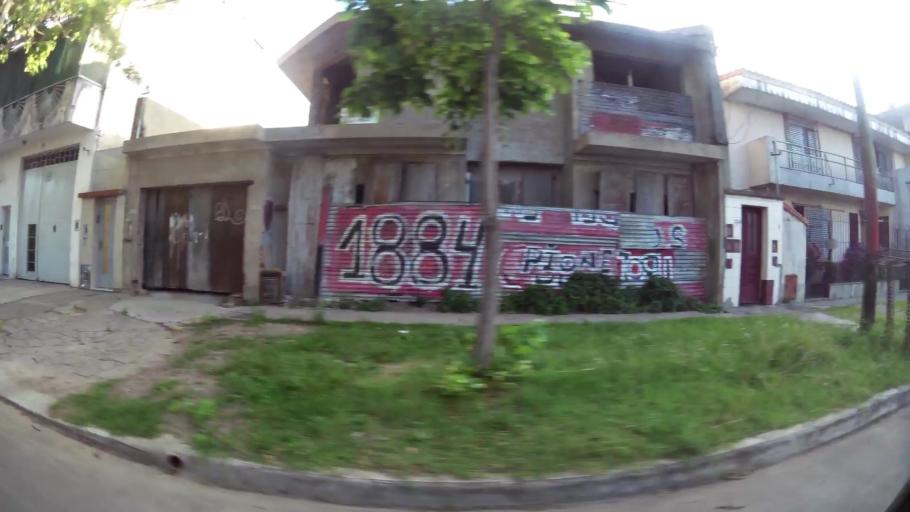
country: AR
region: Santa Fe
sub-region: Departamento de Rosario
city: Rosario
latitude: -32.9680
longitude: -60.6616
